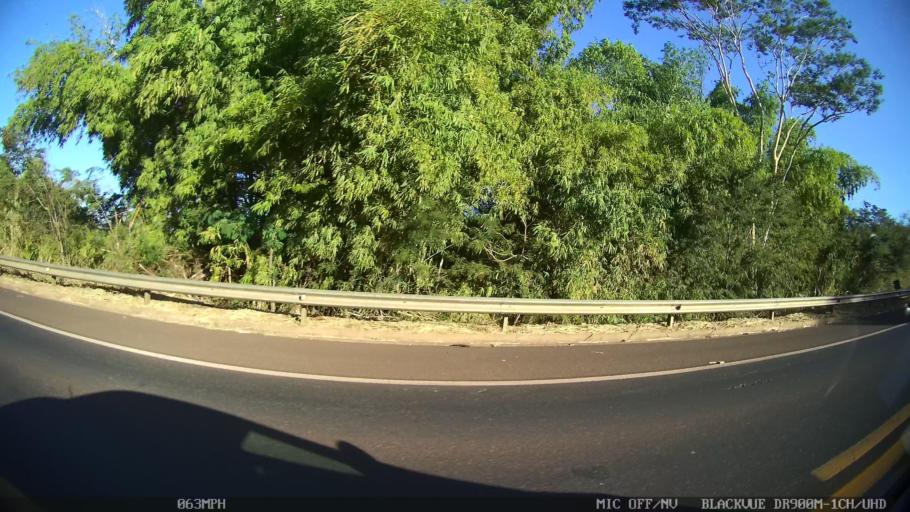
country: BR
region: Sao Paulo
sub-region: Olimpia
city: Olimpia
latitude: -20.7121
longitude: -48.9812
